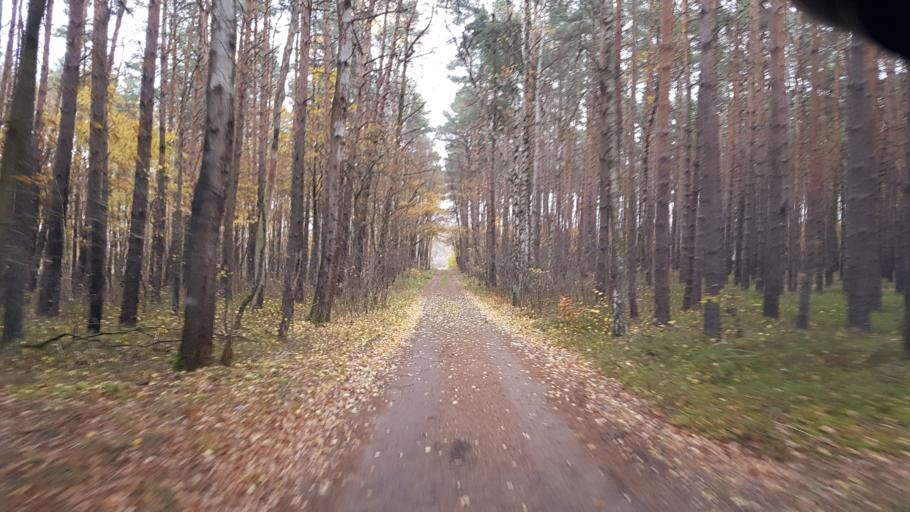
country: DE
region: Brandenburg
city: Sallgast
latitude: 51.6192
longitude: 13.8805
